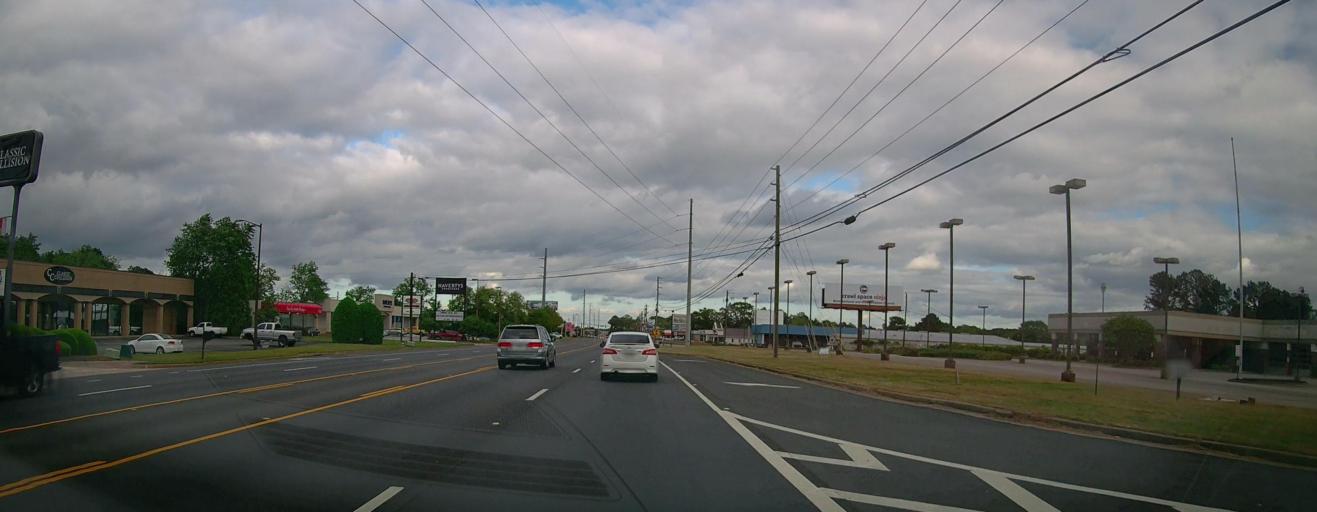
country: US
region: Georgia
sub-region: Oconee County
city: Bogart
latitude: 33.9404
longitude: -83.4800
